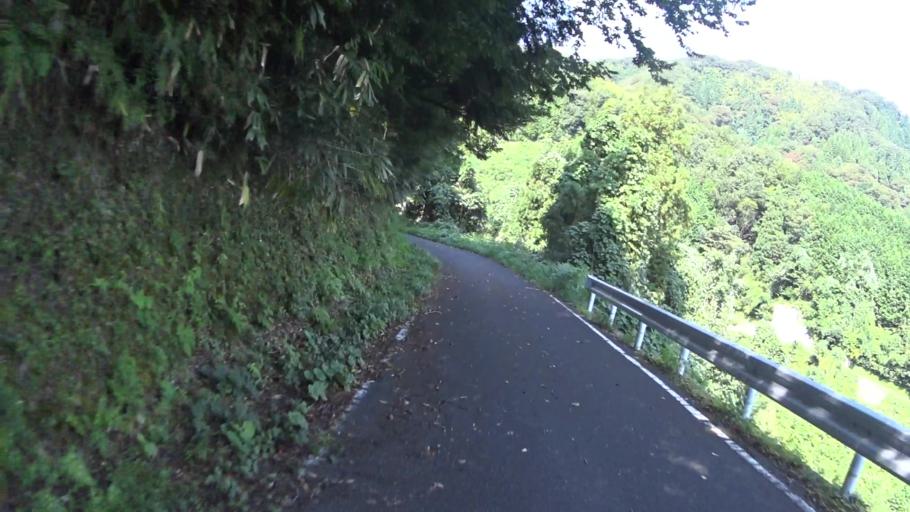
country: JP
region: Kyoto
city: Miyazu
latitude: 35.6552
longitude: 135.2443
